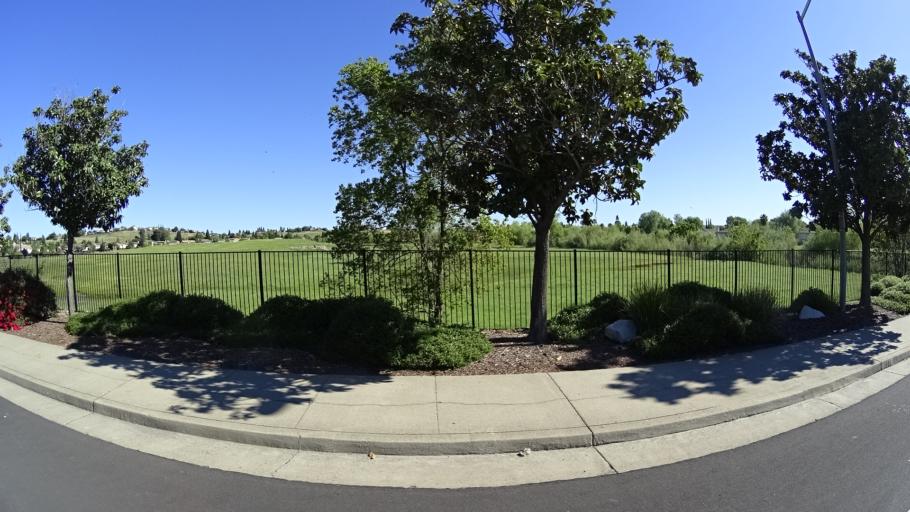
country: US
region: California
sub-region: Placer County
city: Rocklin
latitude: 38.8147
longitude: -121.2654
